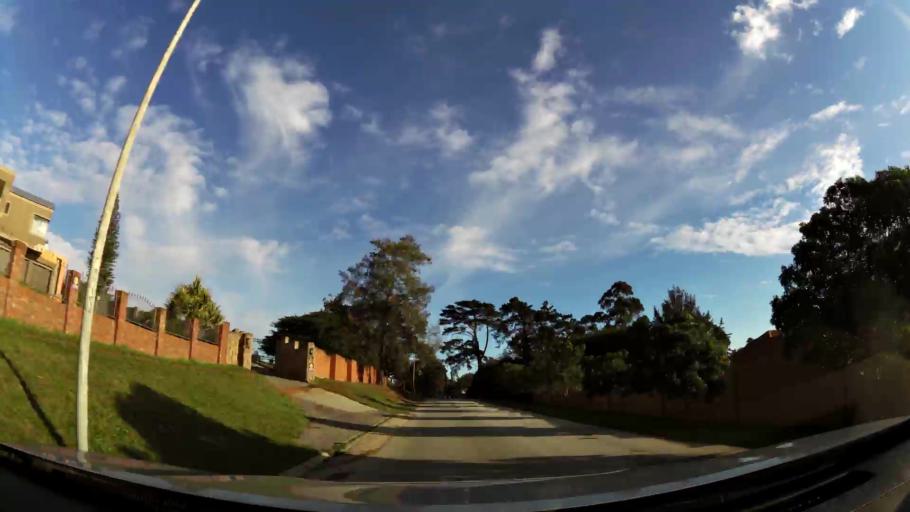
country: ZA
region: Eastern Cape
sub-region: Nelson Mandela Bay Metropolitan Municipality
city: Port Elizabeth
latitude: -33.9641
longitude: 25.5075
